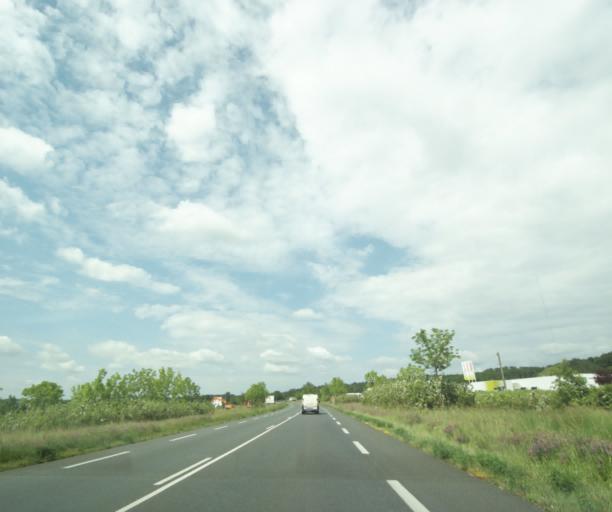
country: FR
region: Pays de la Loire
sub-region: Departement de Maine-et-Loire
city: Distre
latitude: 47.2315
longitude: -0.1131
